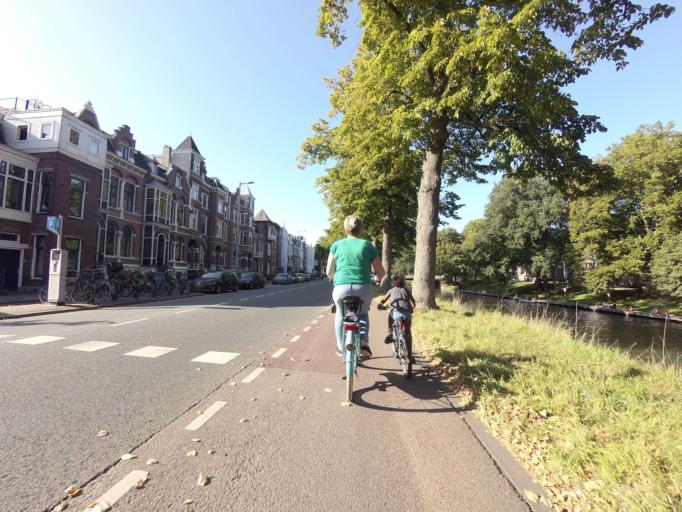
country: NL
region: Utrecht
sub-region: Gemeente Utrecht
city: Utrecht
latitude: 52.0843
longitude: 5.1194
